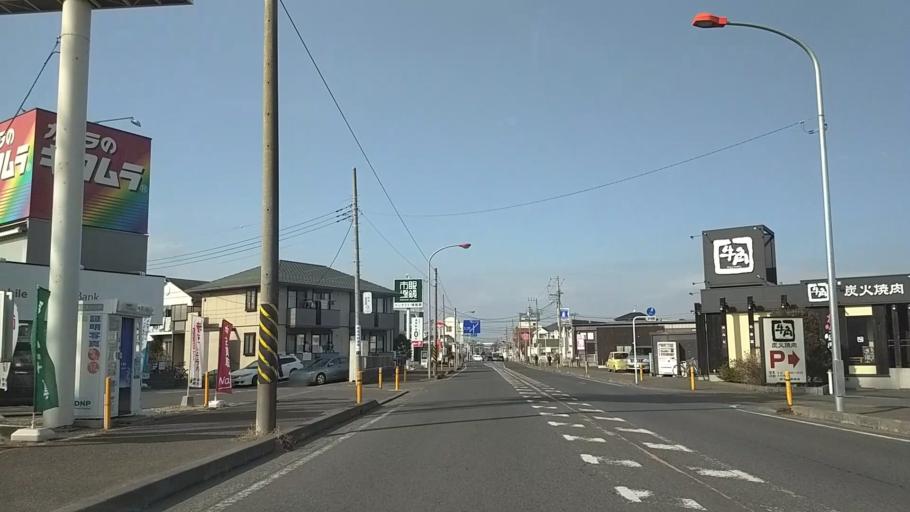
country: JP
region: Kanagawa
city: Chigasaki
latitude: 35.3410
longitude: 139.4128
